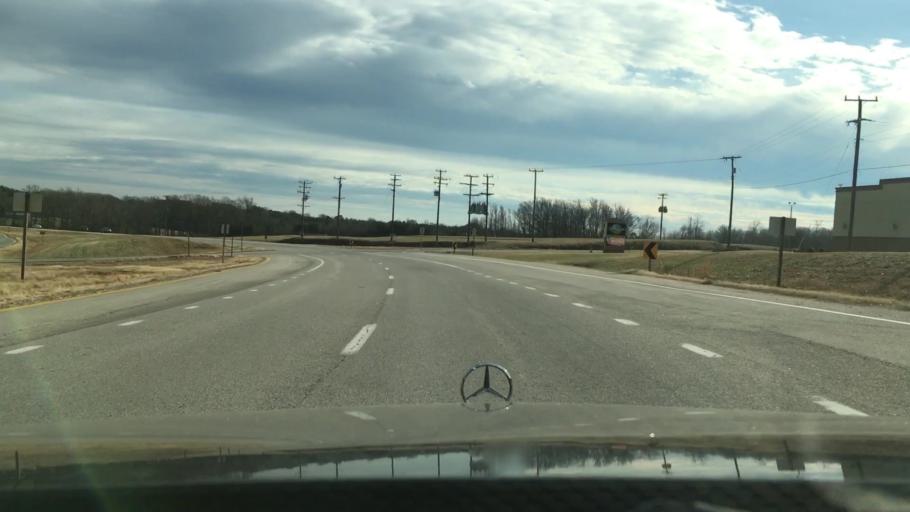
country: US
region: Virginia
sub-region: Pittsylvania County
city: Mount Hermon
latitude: 36.7230
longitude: -79.3854
